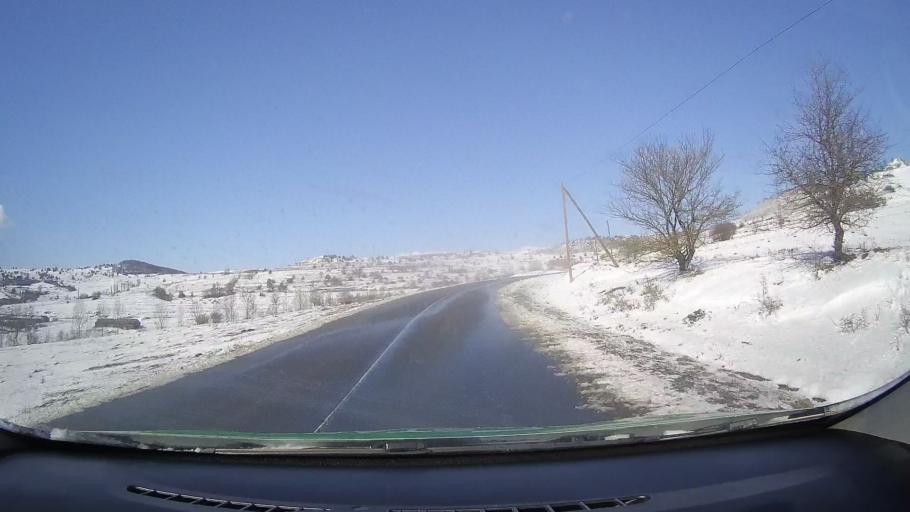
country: RO
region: Sibiu
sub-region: Comuna Avrig
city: Avrig
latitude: 45.7666
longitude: 24.3877
